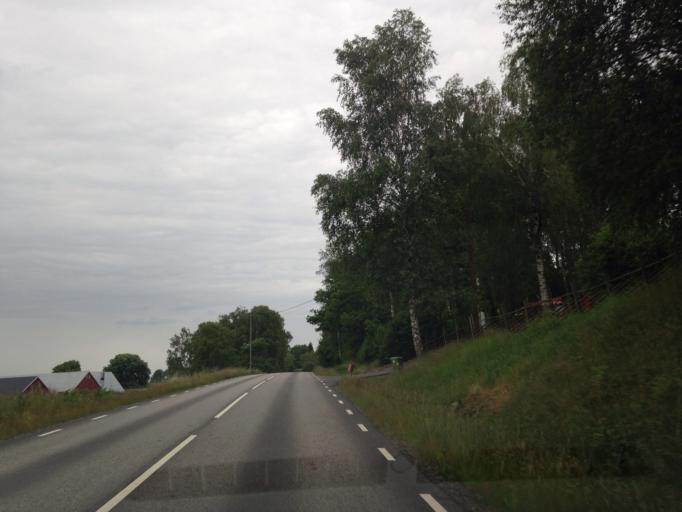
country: SE
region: Vaestra Goetaland
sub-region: Marks Kommun
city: Horred
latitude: 57.4823
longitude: 12.5202
